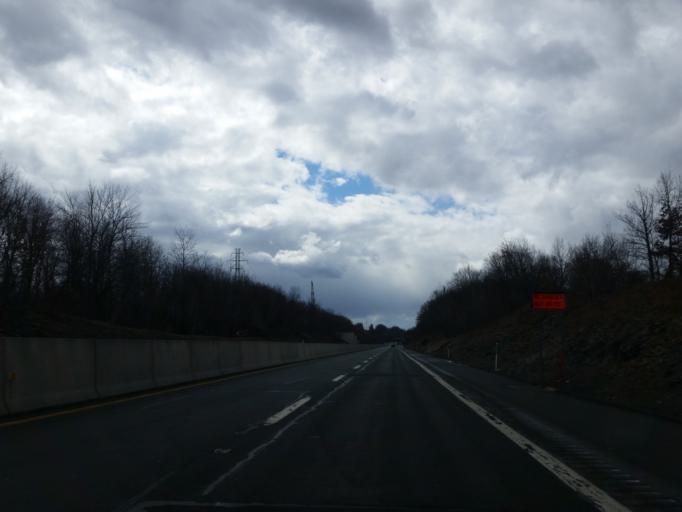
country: US
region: Pennsylvania
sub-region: Luzerne County
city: Avoca
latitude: 41.3258
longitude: -75.7284
